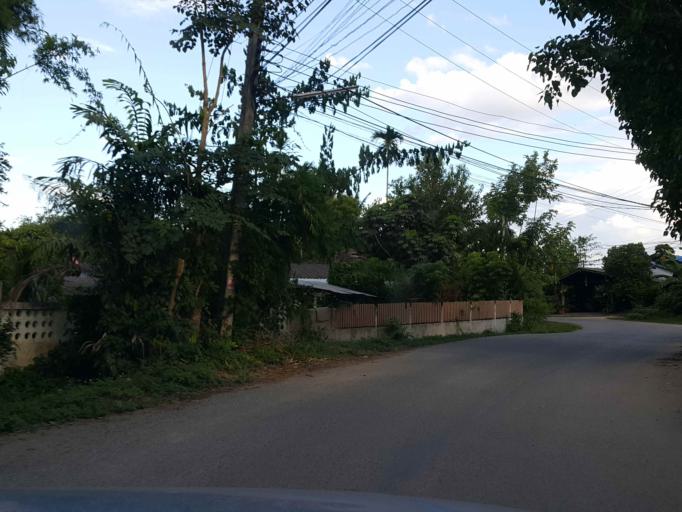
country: TH
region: Chiang Mai
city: San Sai
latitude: 18.8983
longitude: 98.9858
